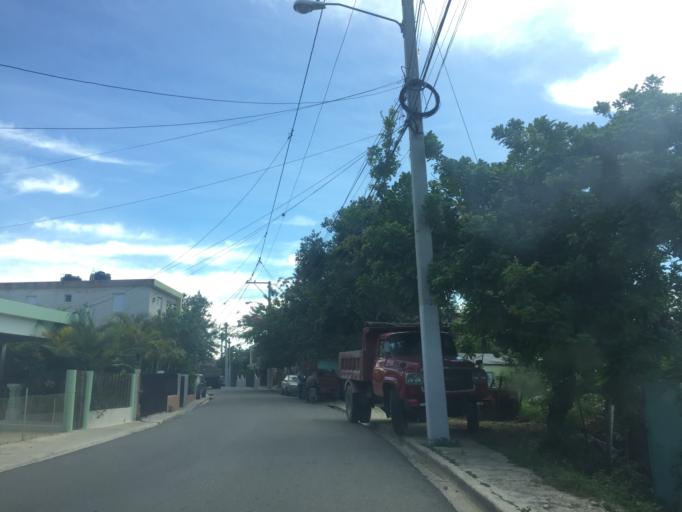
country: DO
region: Santiago
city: Santiago de los Caballeros
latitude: 19.4325
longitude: -70.6765
